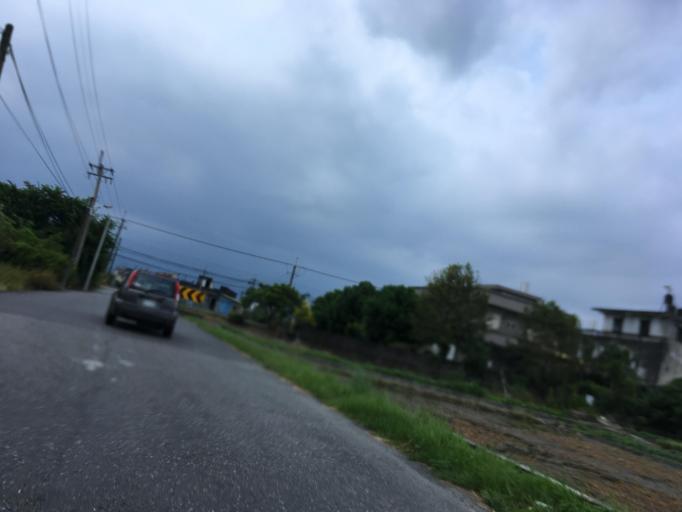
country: TW
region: Taiwan
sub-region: Yilan
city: Yilan
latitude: 24.7002
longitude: 121.7429
